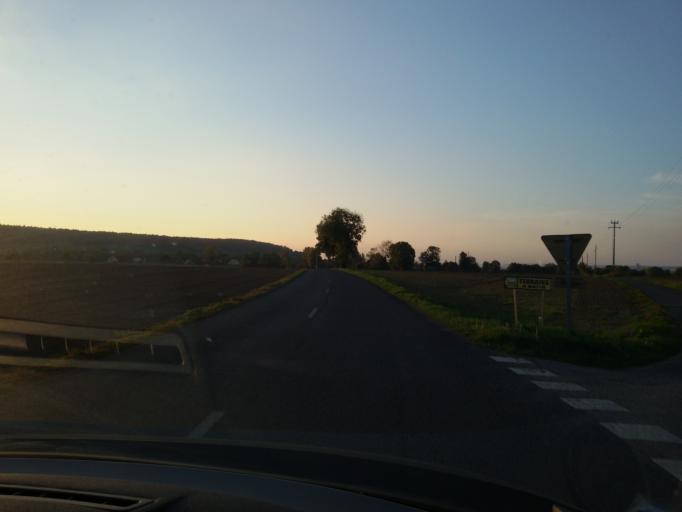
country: FR
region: Haute-Normandie
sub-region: Departement de l'Eure
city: Beuzeville
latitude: 49.4249
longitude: 0.3770
